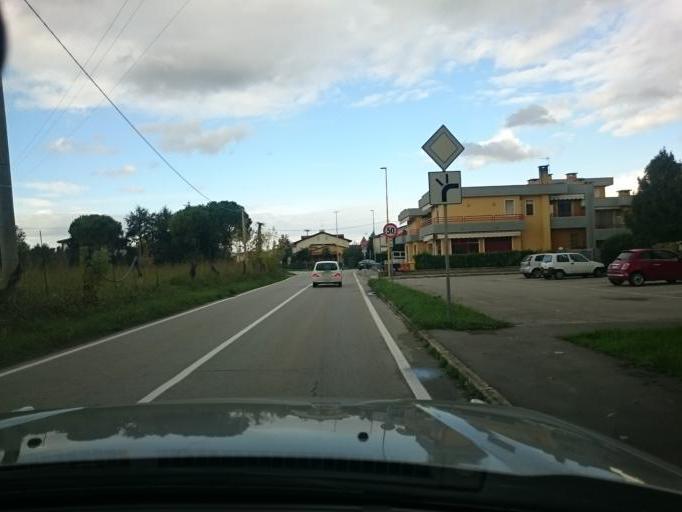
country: IT
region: Veneto
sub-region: Provincia di Padova
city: Ponte San Nicolo
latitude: 45.3615
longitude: 11.9056
